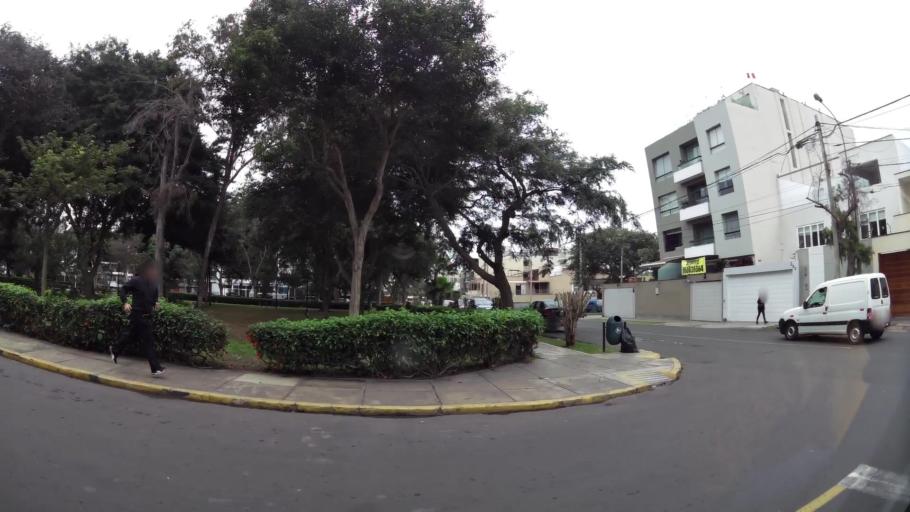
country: PE
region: Lima
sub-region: Lima
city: Surco
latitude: -12.1215
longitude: -77.0172
